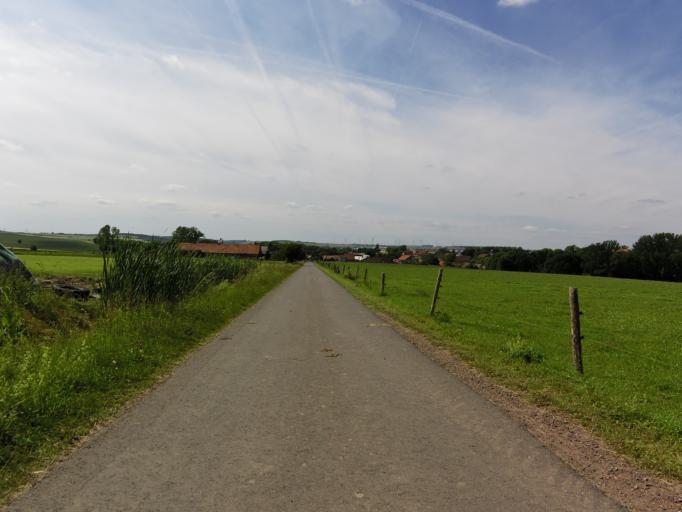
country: DE
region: Thuringia
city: Seebach
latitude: 50.9763
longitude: 10.4372
